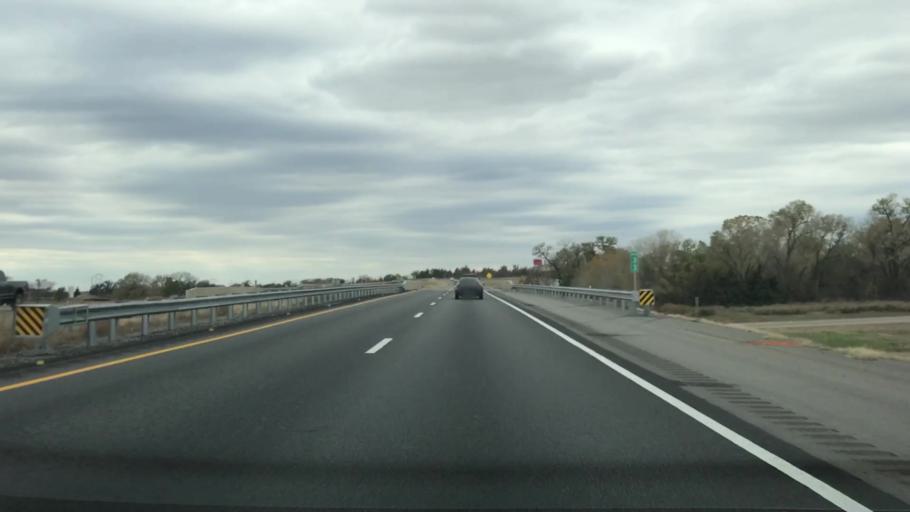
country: US
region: Oklahoma
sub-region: Beckham County
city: Elk City
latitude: 35.3858
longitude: -99.5044
